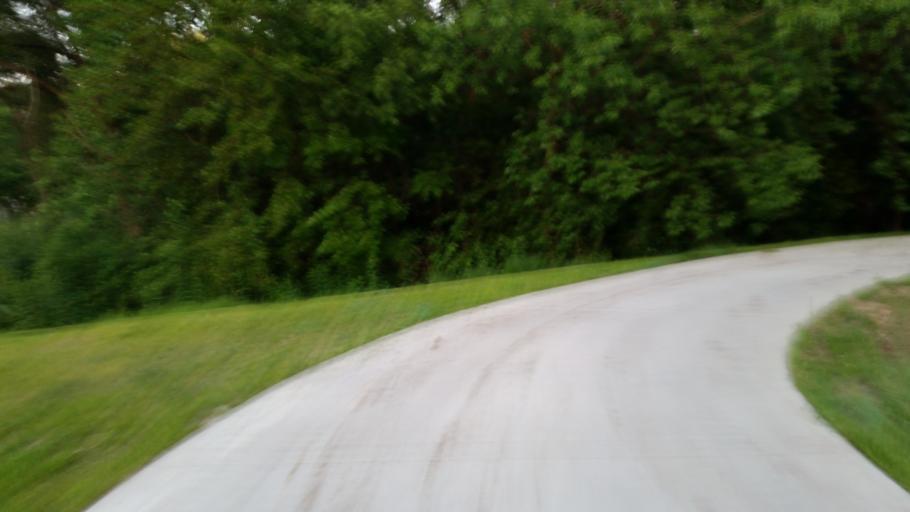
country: US
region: Nebraska
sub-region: Sarpy County
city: Offutt Air Force Base
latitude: 41.1119
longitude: -95.9470
